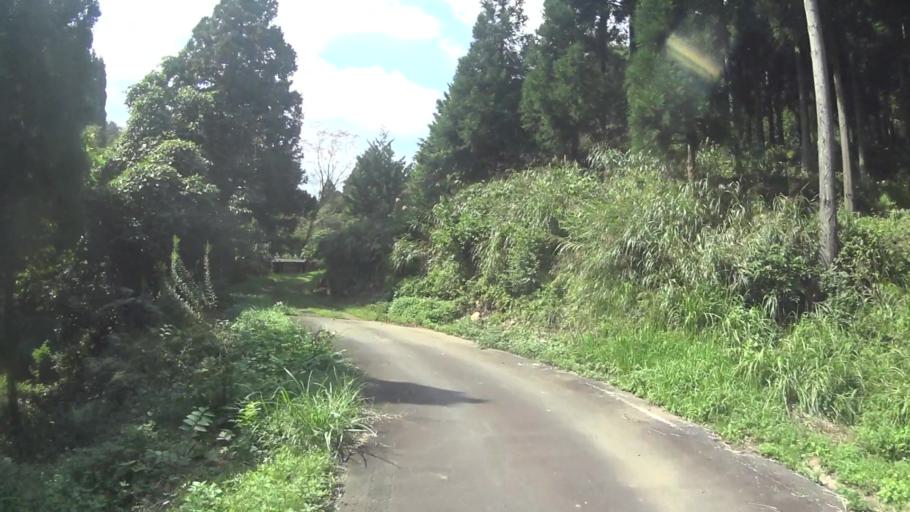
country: JP
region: Kyoto
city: Miyazu
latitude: 35.7428
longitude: 135.1874
